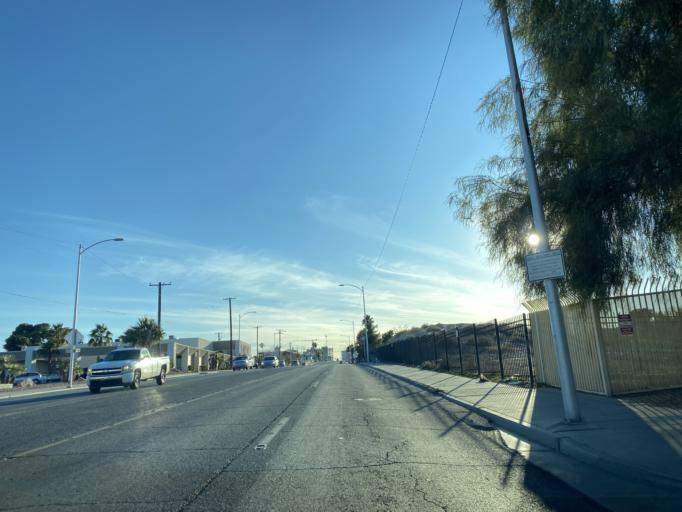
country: US
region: Nevada
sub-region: Clark County
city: Las Vegas
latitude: 36.1862
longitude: -115.1369
